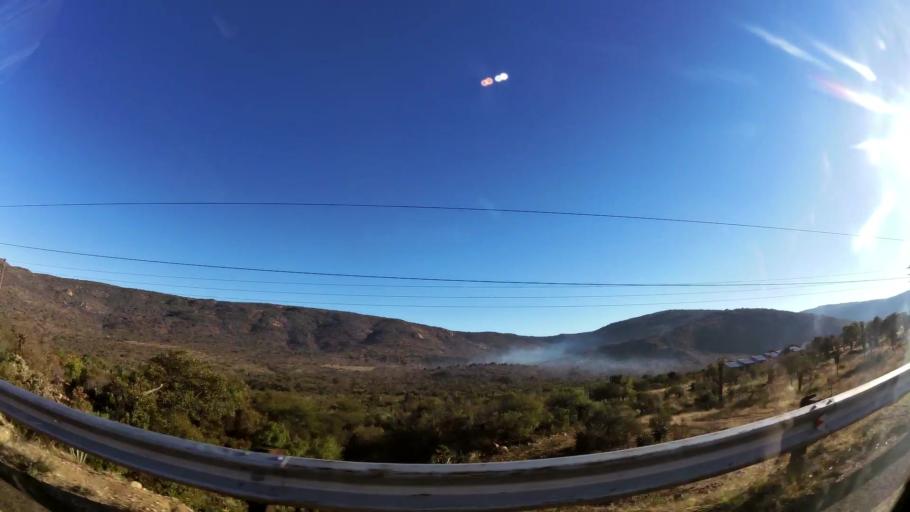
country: ZA
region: Limpopo
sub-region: Capricorn District Municipality
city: Mankoeng
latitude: -23.9344
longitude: 29.8365
